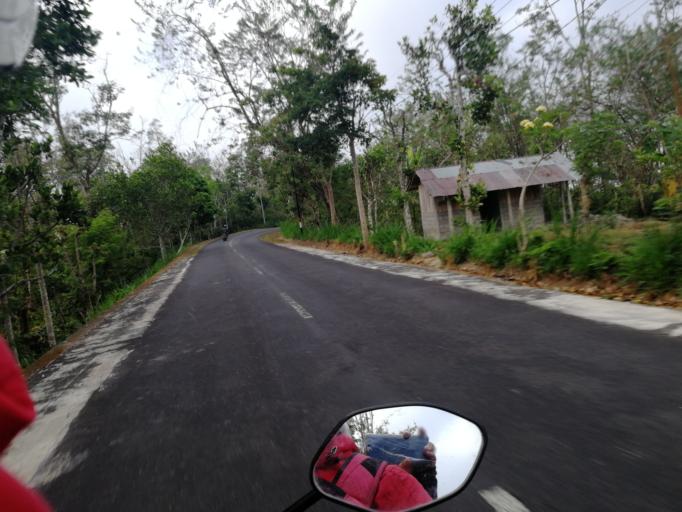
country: ID
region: Bali
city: Banjar Taro Kelod
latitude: -8.2540
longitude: 115.2453
